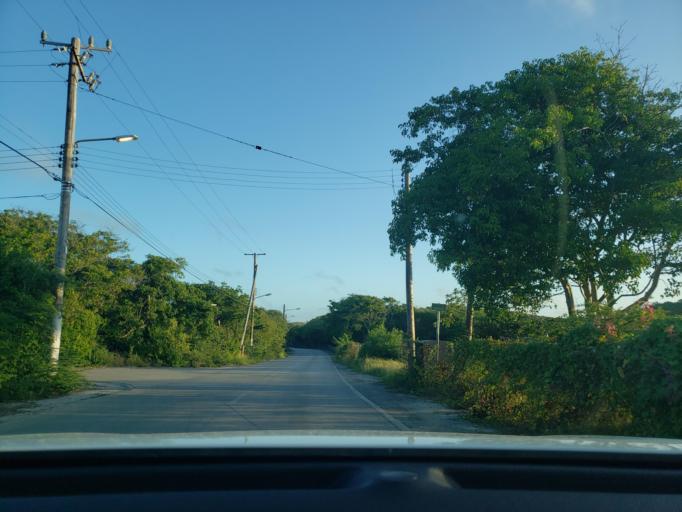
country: CW
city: Barber
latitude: 12.2655
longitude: -69.0666
